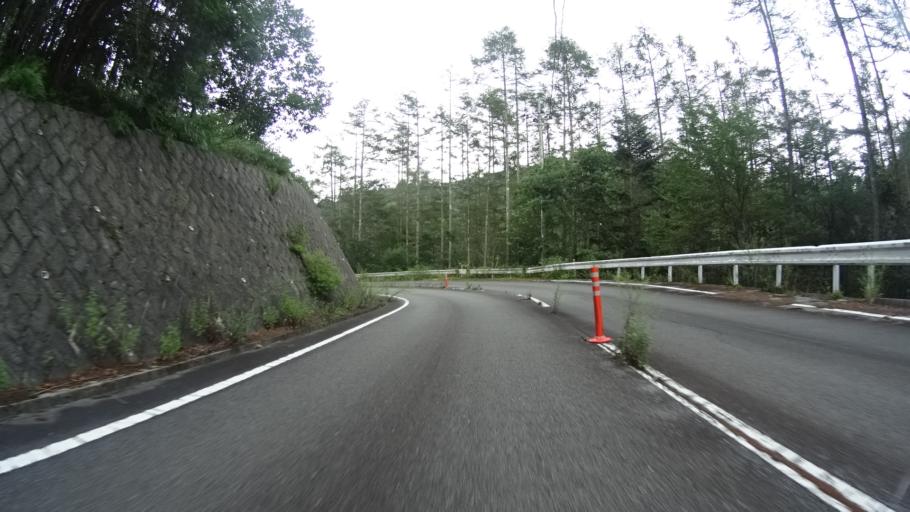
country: JP
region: Yamanashi
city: Enzan
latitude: 35.8000
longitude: 138.6509
